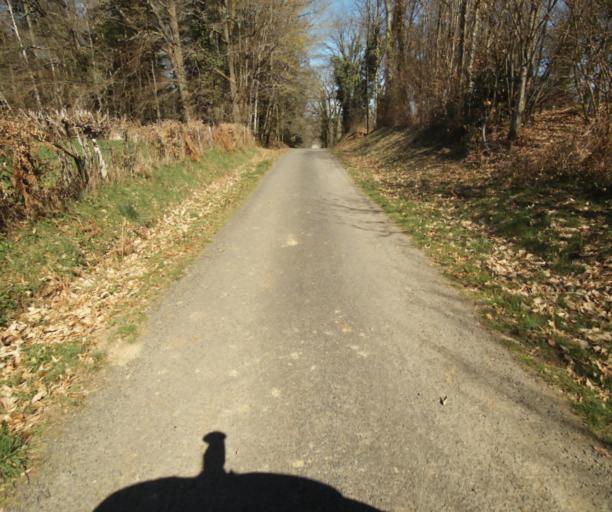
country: FR
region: Limousin
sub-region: Departement de la Correze
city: Saint-Clement
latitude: 45.3961
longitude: 1.6392
